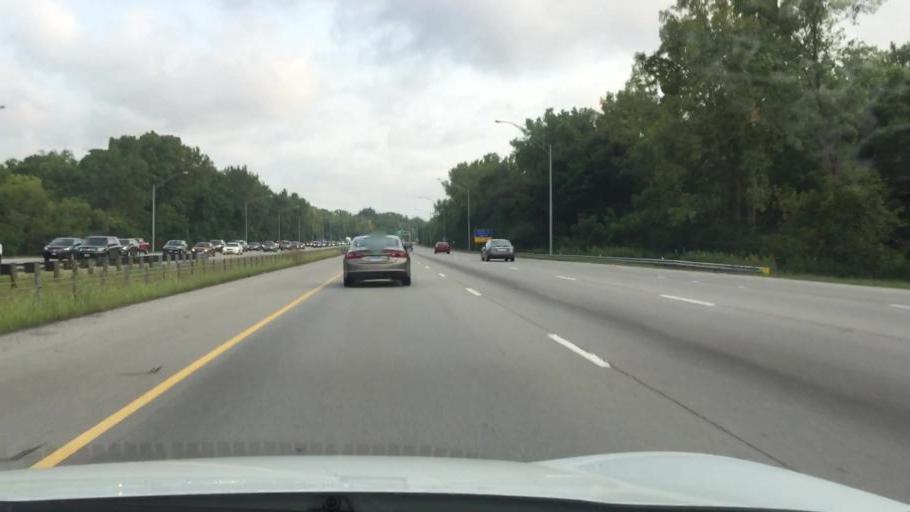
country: US
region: Ohio
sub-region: Franklin County
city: Worthington
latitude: 40.0671
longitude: -83.0332
